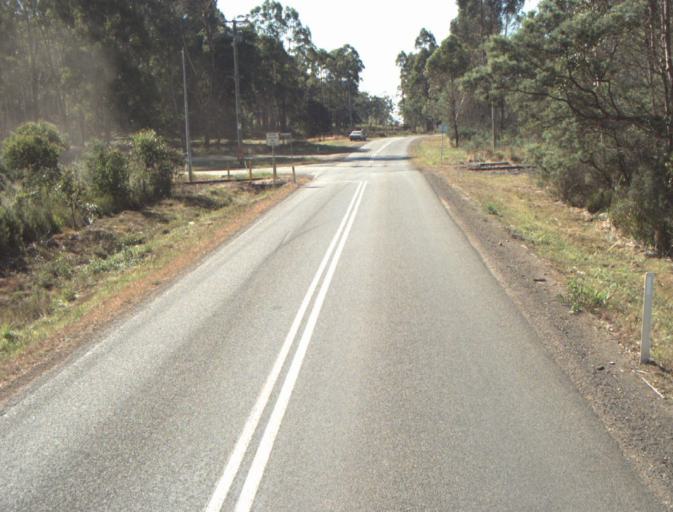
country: AU
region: Tasmania
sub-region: Launceston
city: Mayfield
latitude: -41.2826
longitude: 147.1260
